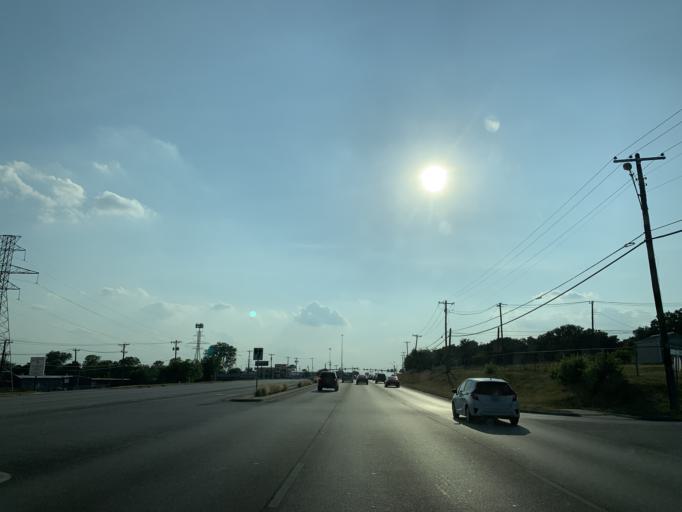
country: US
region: Texas
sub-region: Tarrant County
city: Richland Hills
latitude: 32.8090
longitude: -97.2027
